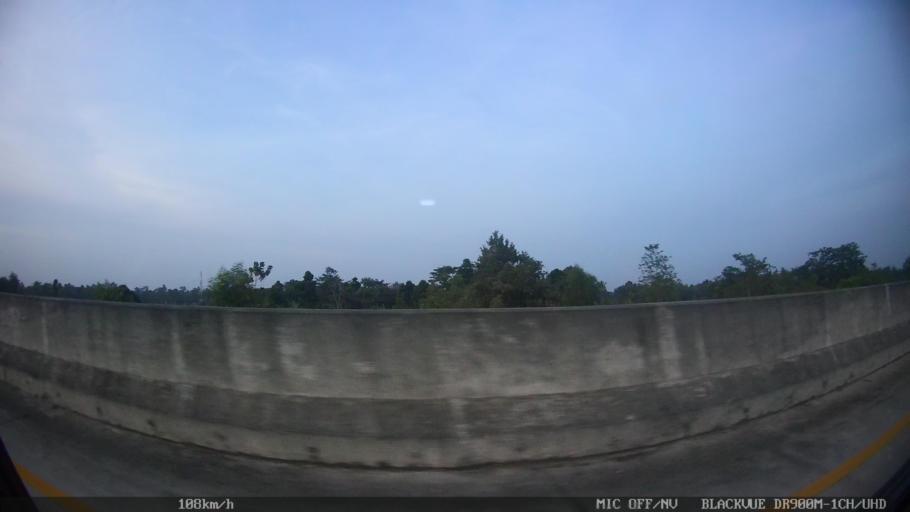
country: ID
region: Lampung
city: Pasuruan
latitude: -5.7438
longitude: 105.6975
